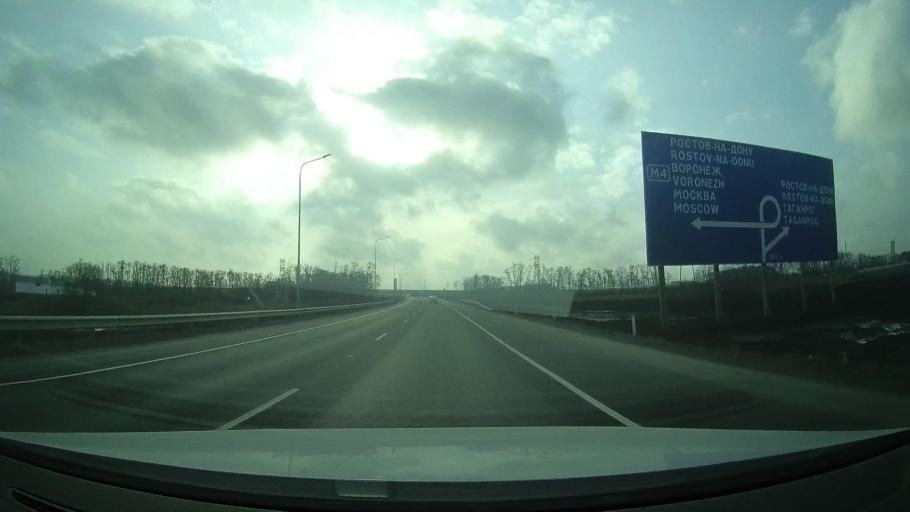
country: RU
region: Rostov
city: Grushevskaya
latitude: 47.3866
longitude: 39.8457
